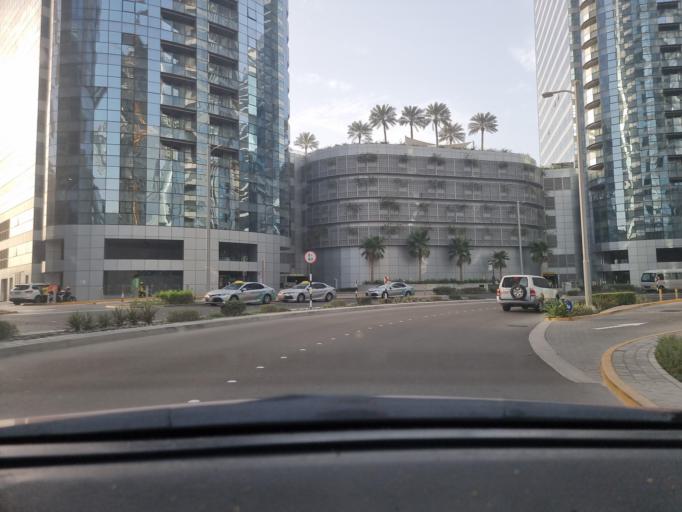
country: AE
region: Abu Dhabi
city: Abu Dhabi
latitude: 24.4988
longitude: 54.4036
